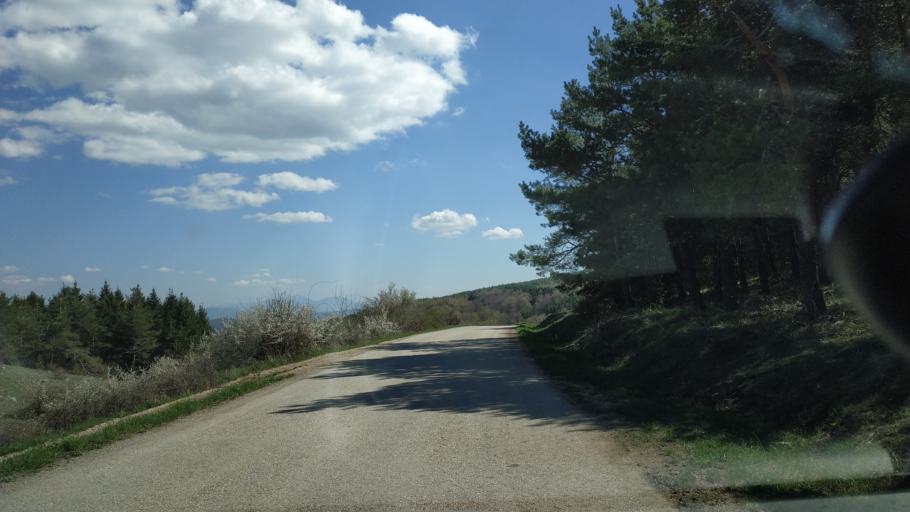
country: RS
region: Central Serbia
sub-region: Zajecarski Okrug
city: Soko Banja
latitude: 43.5904
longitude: 21.8880
